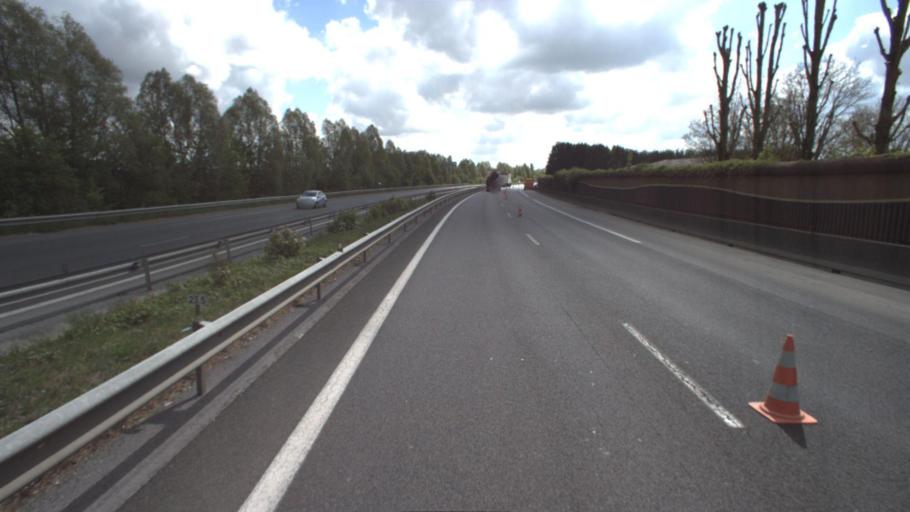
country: FR
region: Ile-de-France
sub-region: Departement de Seine-et-Marne
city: Fontenay-Tresigny
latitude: 48.7114
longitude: 2.8744
